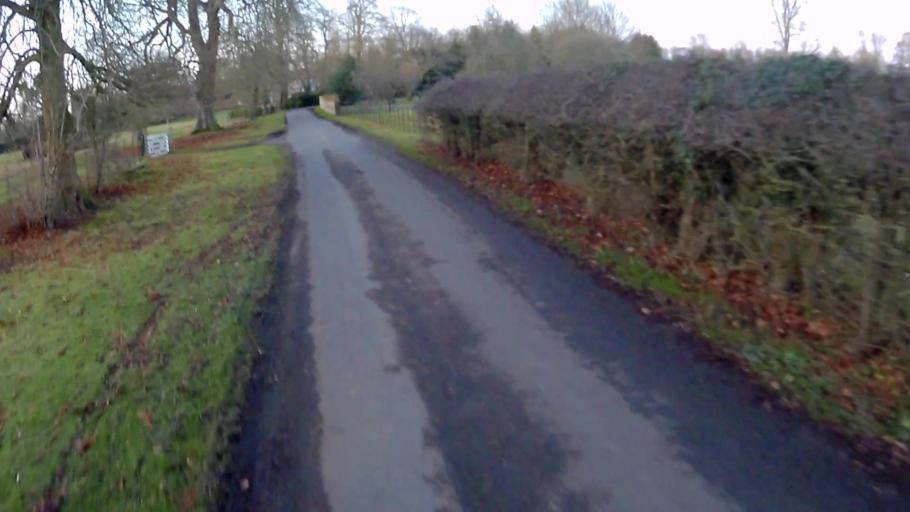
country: GB
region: England
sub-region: Hampshire
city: Overton
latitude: 51.2473
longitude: -1.2174
